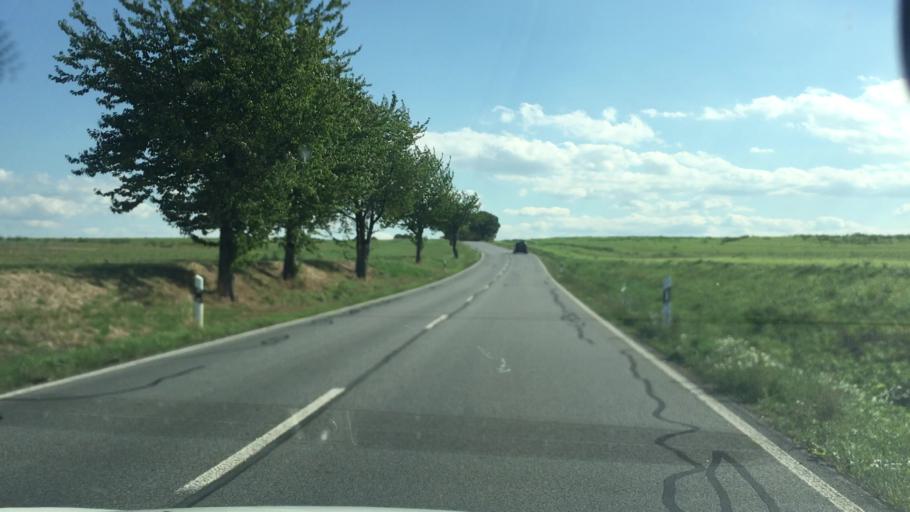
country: DE
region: Saxony
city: Dohma
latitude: 50.9290
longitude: 13.9295
